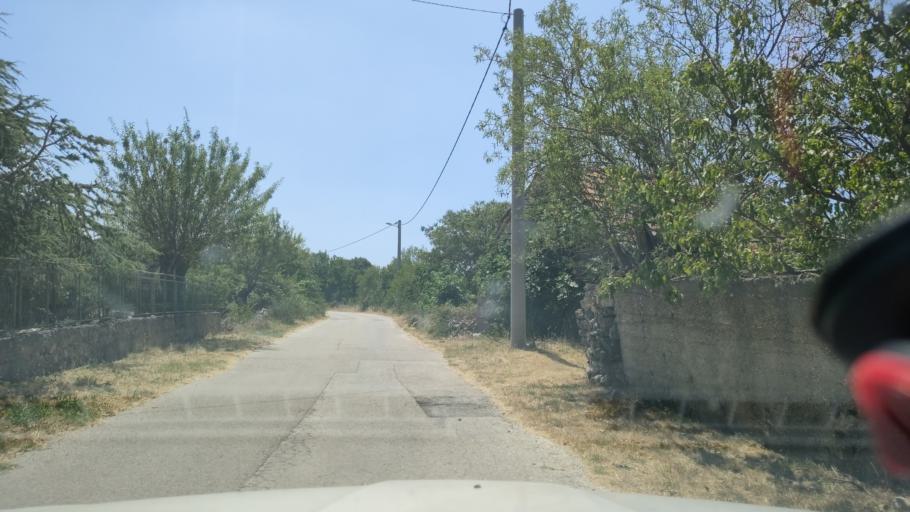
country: HR
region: Sibensko-Kniniska
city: Kistanje
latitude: 43.9498
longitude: 15.8828
